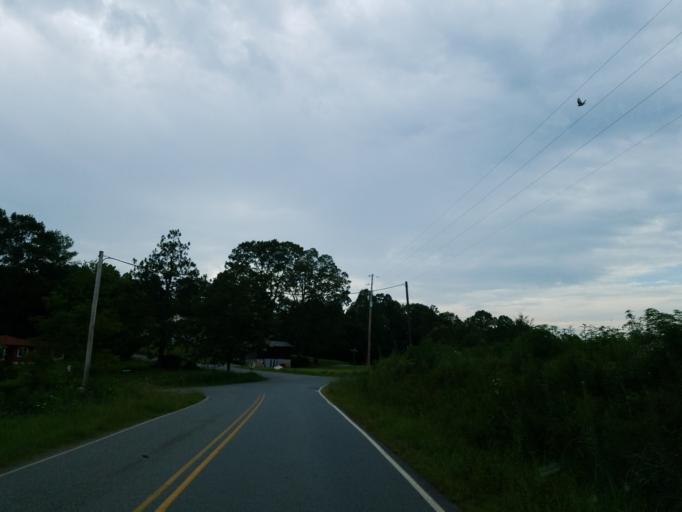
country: US
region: Georgia
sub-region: Fannin County
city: Blue Ridge
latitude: 34.8478
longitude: -84.2292
